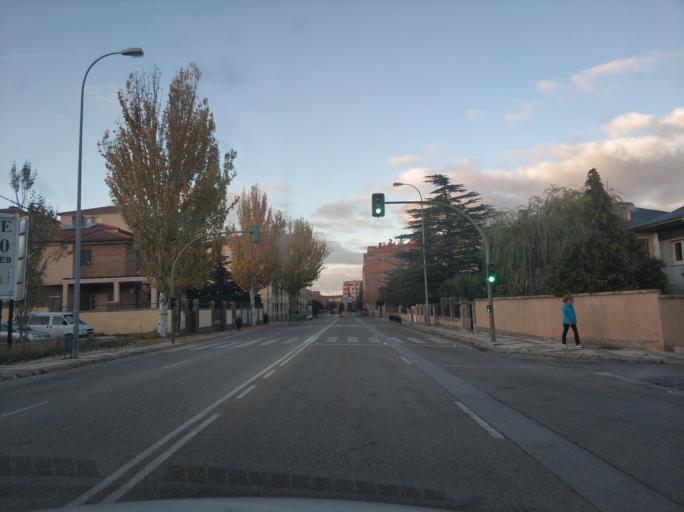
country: ES
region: Castille and Leon
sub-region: Provincia de Soria
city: Soria
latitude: 41.7642
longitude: -2.4787
